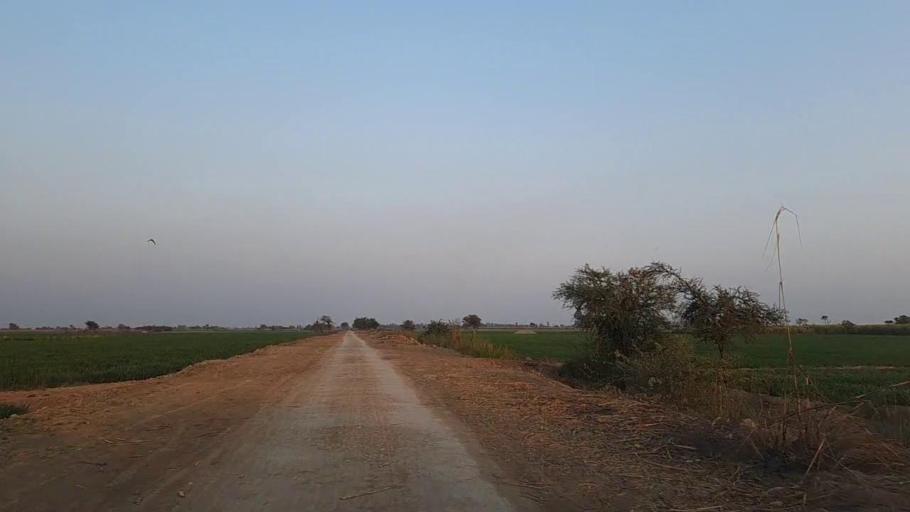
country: PK
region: Sindh
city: Jam Sahib
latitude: 26.3050
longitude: 68.5632
